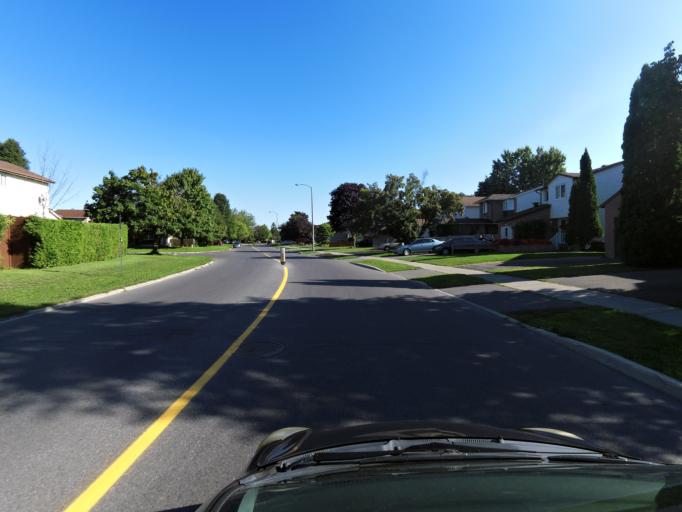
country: CA
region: Quebec
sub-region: Outaouais
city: Gatineau
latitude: 45.4640
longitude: -75.4942
